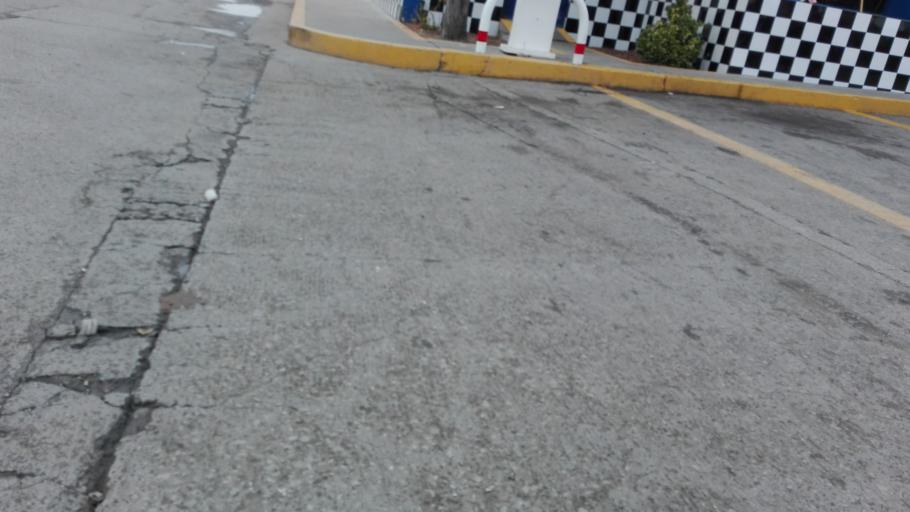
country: MX
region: Chihuahua
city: Ciudad Juarez
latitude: 31.7217
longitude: -106.4181
